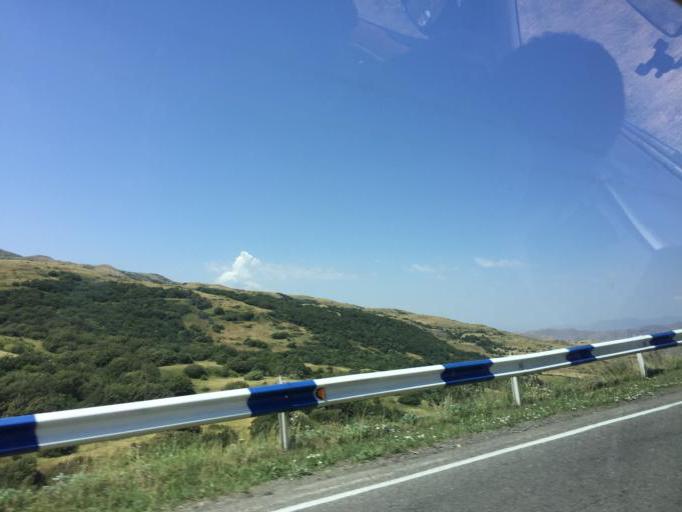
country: AM
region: Vayots' Dzori Marz
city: Jermuk
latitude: 39.7058
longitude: 45.6750
